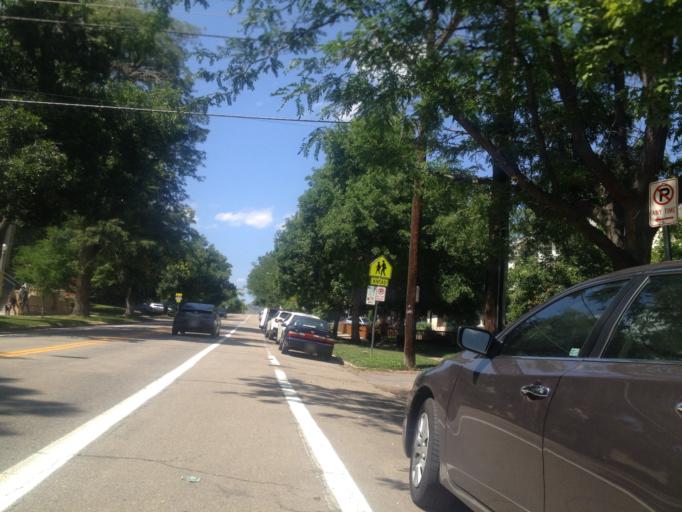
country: US
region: Colorado
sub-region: Boulder County
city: Boulder
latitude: 40.0205
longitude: -105.2795
